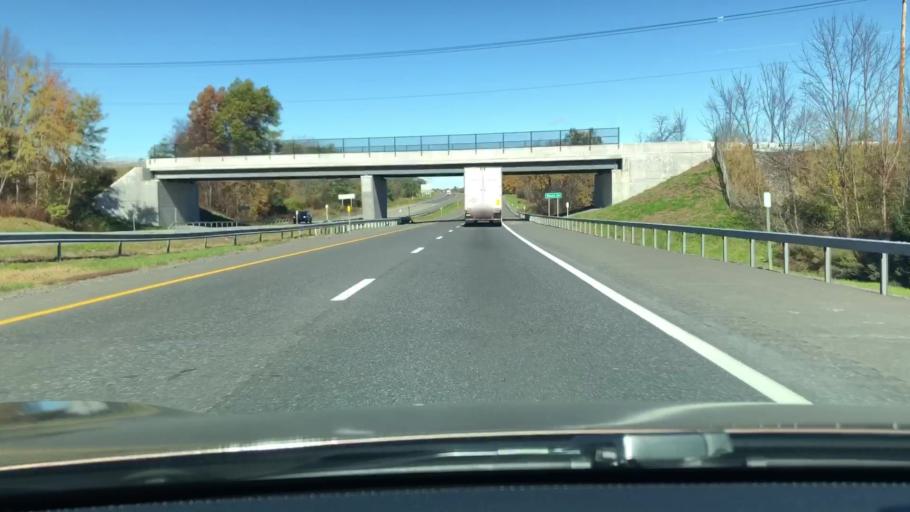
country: US
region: New York
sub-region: Ulster County
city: Plattekill
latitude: 41.6199
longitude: -74.0810
